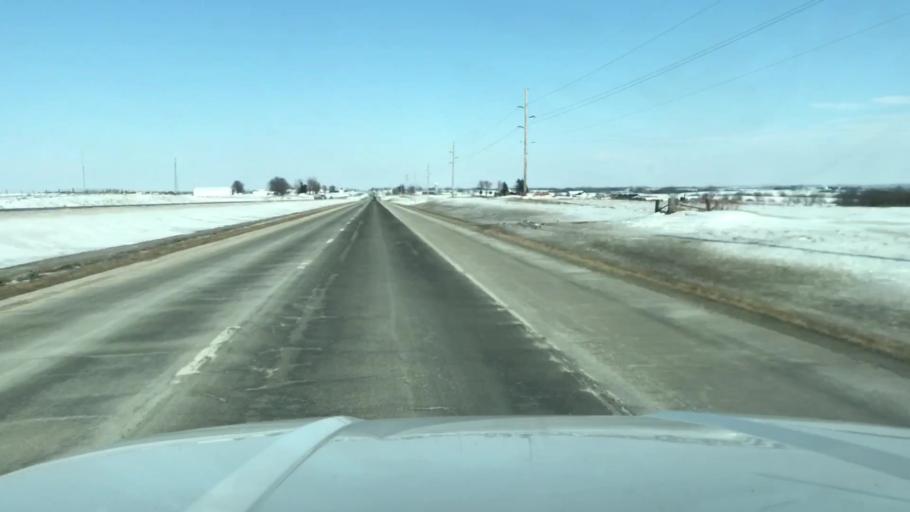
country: US
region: Missouri
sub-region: Nodaway County
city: Maryville
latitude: 40.2312
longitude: -94.8676
